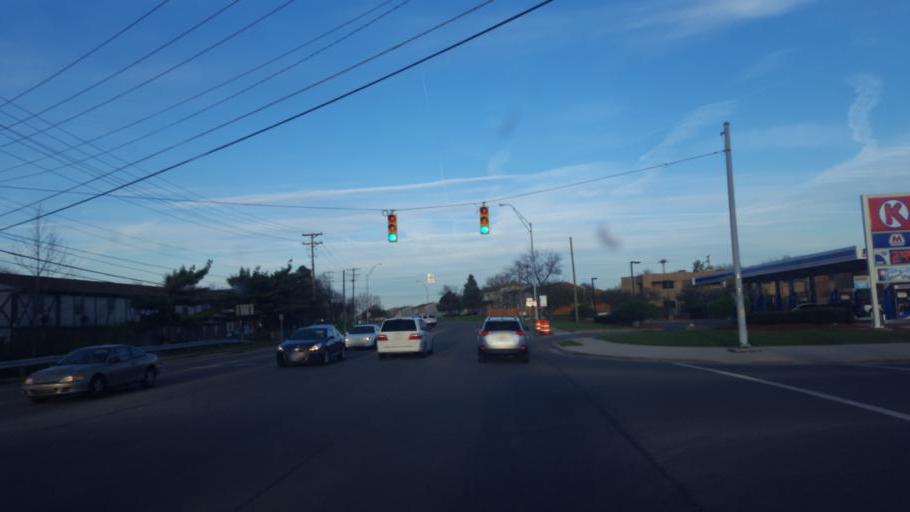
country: US
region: Ohio
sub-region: Franklin County
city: Minerva Park
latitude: 40.1052
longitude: -82.9748
